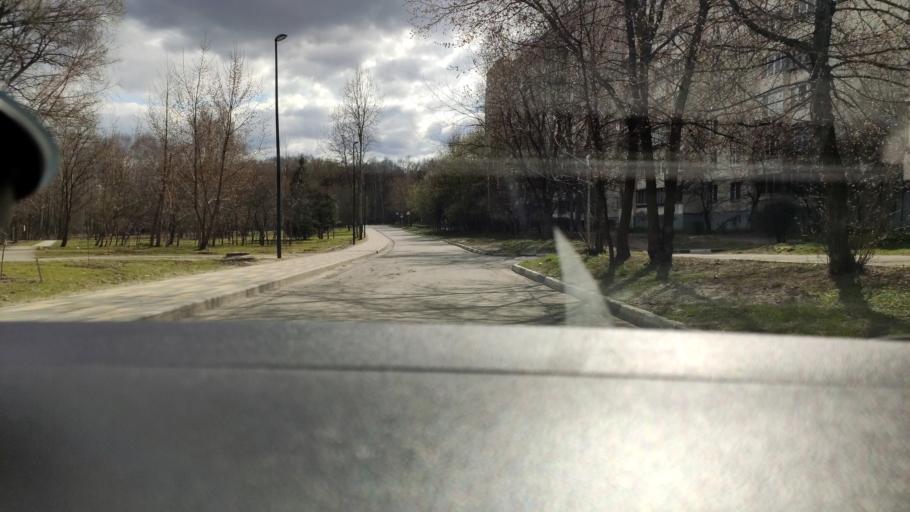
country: RU
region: Moskovskaya
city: Balashikha
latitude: 55.8219
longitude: 37.9579
